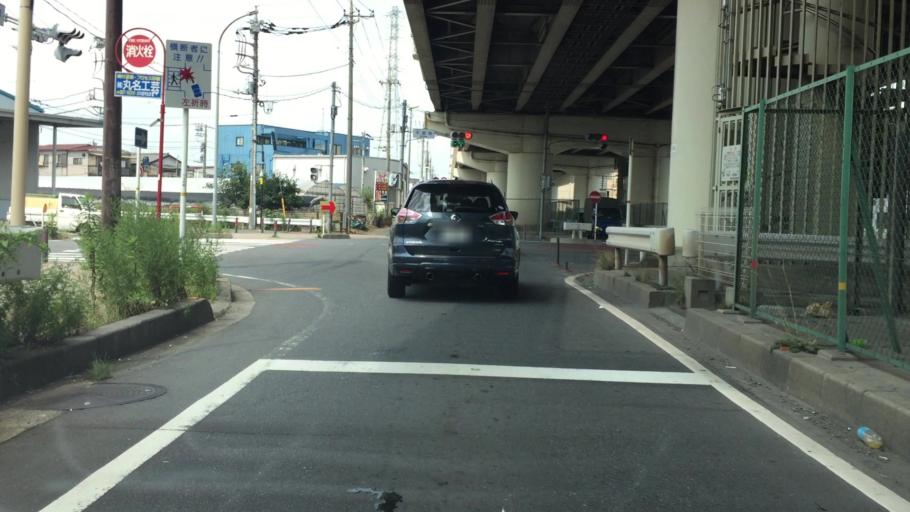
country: JP
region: Saitama
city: Yashio-shi
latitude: 35.8181
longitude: 139.8482
